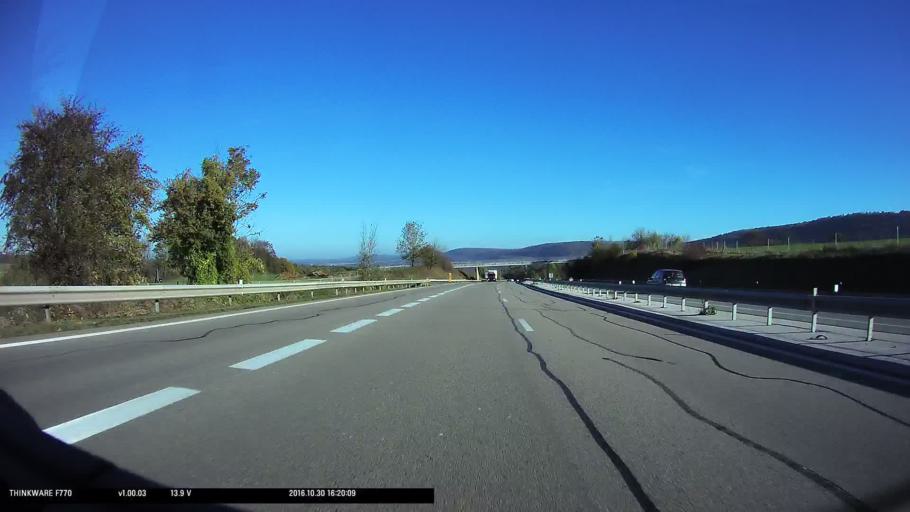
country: FR
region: Franche-Comte
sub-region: Departement du Doubs
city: Clerval
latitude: 47.4074
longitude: 6.4591
